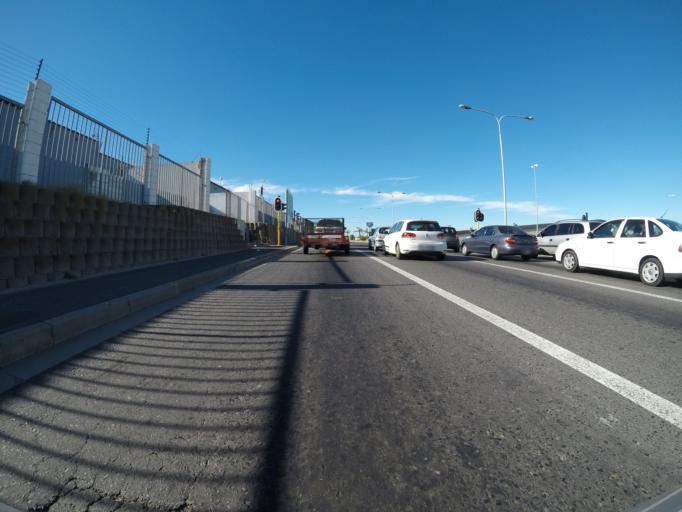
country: ZA
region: Western Cape
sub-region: City of Cape Town
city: Kraaifontein
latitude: -33.9064
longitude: 18.6671
